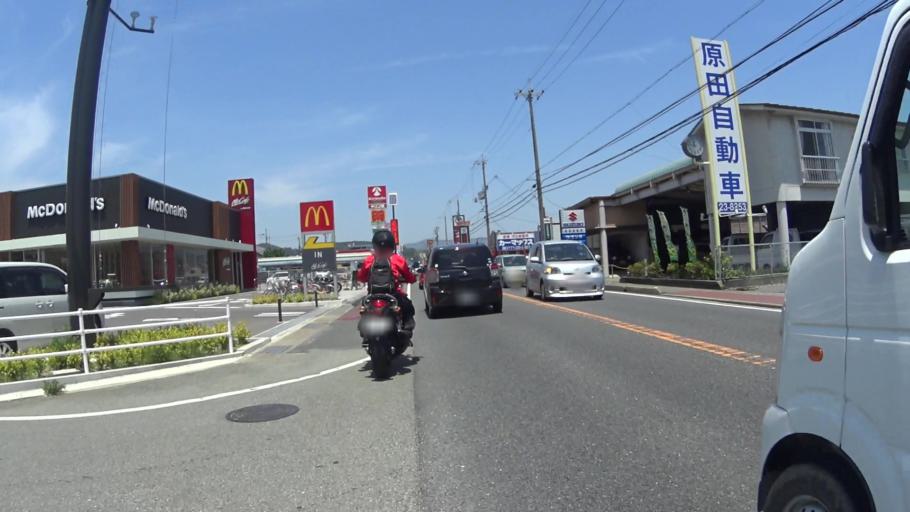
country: JP
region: Kyoto
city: Kameoka
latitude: 35.0415
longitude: 135.5464
